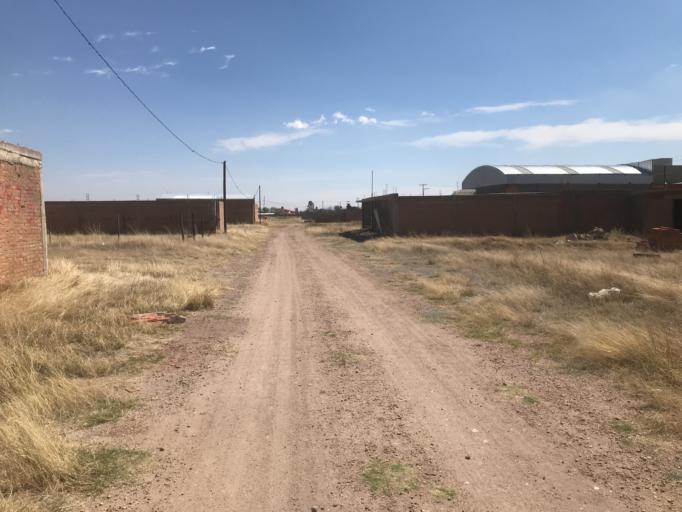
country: MX
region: Durango
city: Victoria de Durango
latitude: 24.0230
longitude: -104.5909
